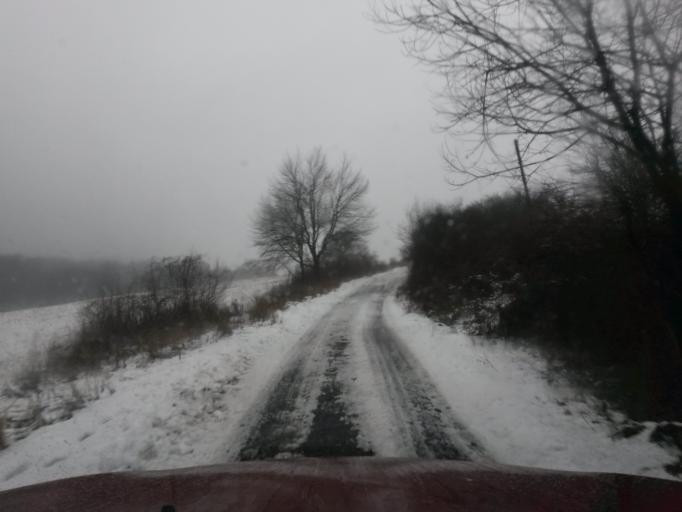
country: SK
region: Presovsky
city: Stropkov
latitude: 49.2534
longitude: 21.7527
